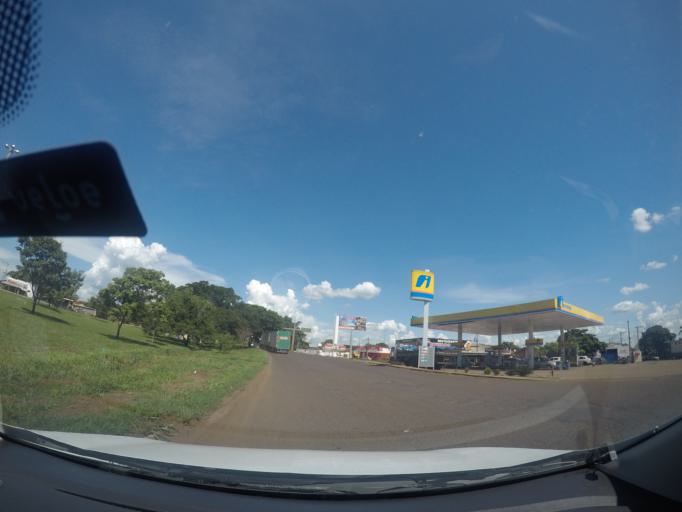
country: BR
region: Minas Gerais
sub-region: Frutal
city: Frutal
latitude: -20.1359
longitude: -48.7014
